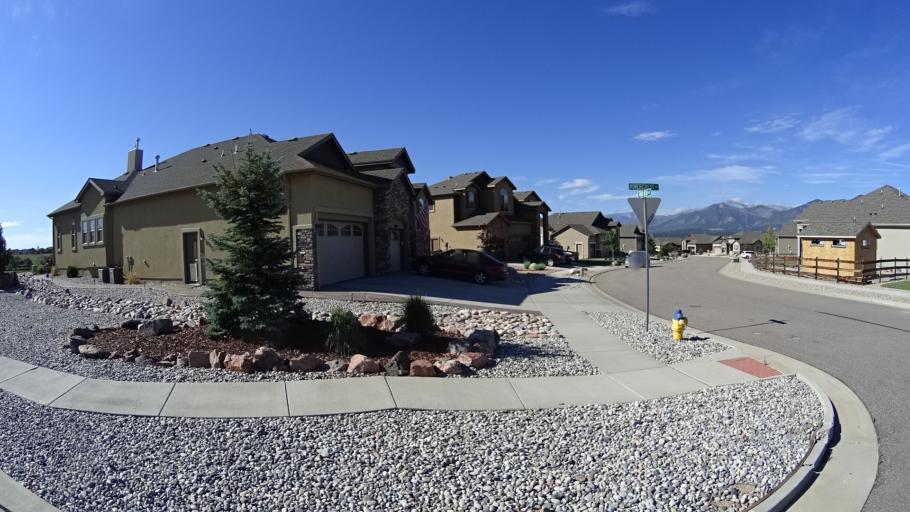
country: US
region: Colorado
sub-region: El Paso County
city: Gleneagle
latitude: 39.0342
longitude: -104.8240
